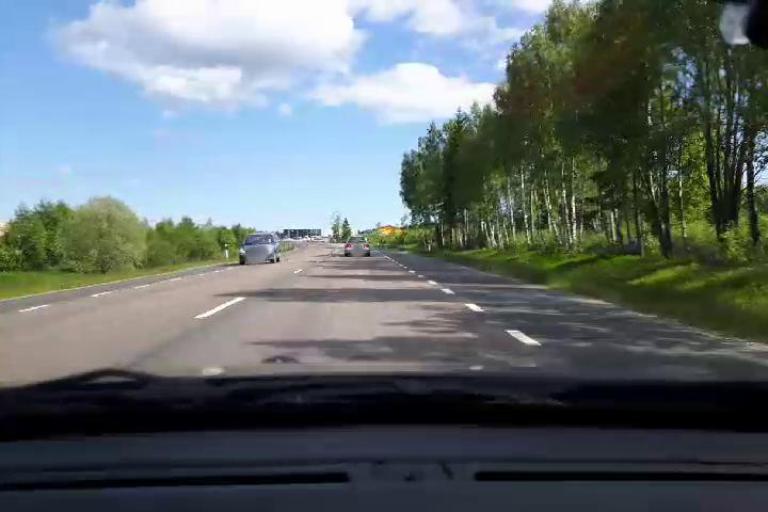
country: SE
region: Gaevleborg
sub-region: Hudiksvalls Kommun
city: Sorforsa
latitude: 61.7158
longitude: 17.0360
